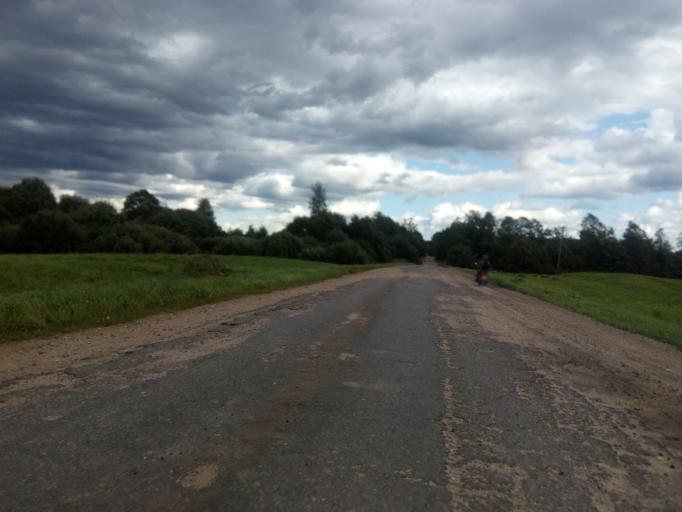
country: BY
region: Vitebsk
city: Dzisna
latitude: 55.7082
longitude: 28.3124
